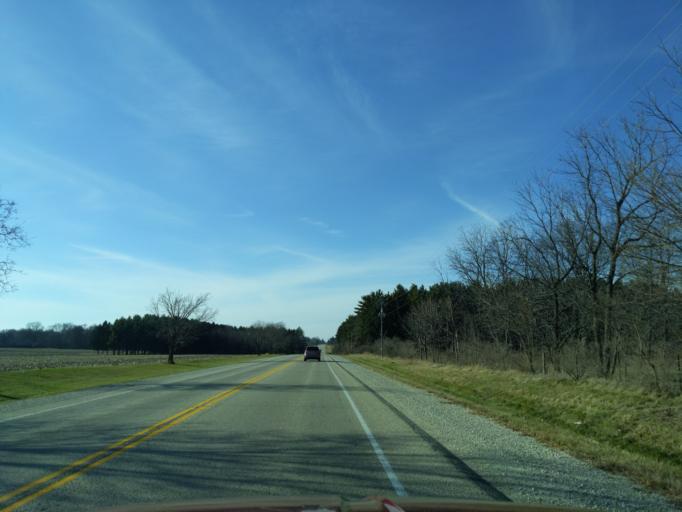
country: US
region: Wisconsin
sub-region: Walworth County
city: Whitewater
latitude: 42.8274
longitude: -88.7835
